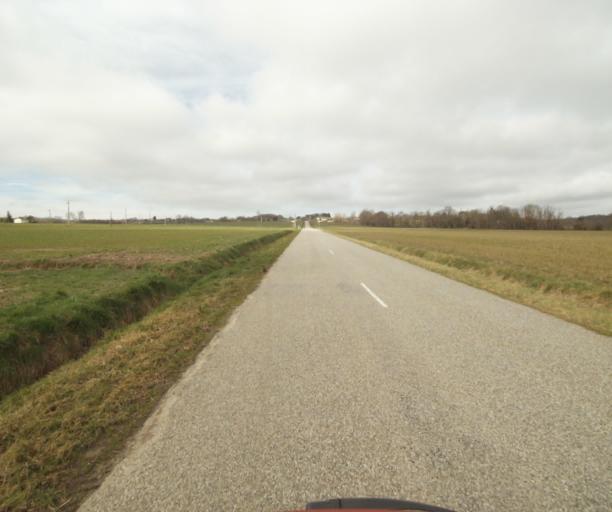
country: FR
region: Midi-Pyrenees
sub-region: Departement de l'Ariege
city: Pamiers
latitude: 43.1082
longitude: 1.5364
